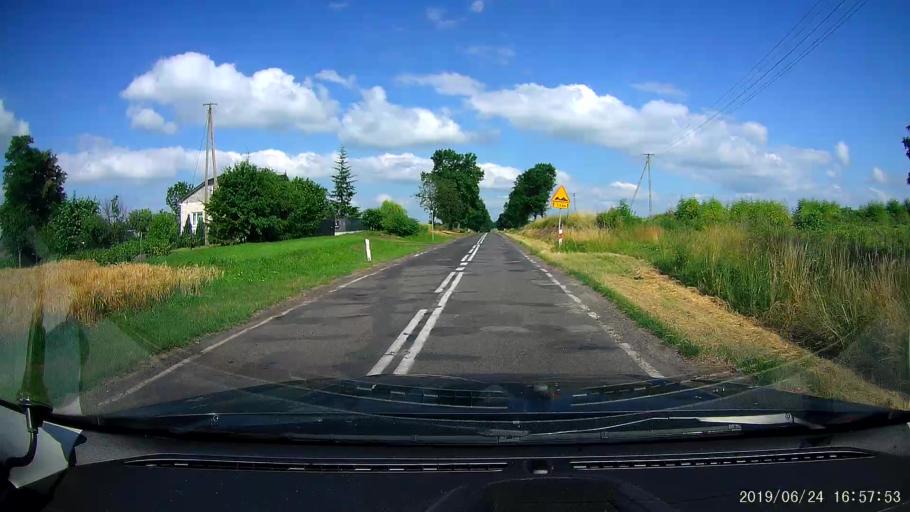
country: PL
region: Lublin Voivodeship
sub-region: Powiat tomaszowski
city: Telatyn
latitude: 50.5259
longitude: 23.8671
